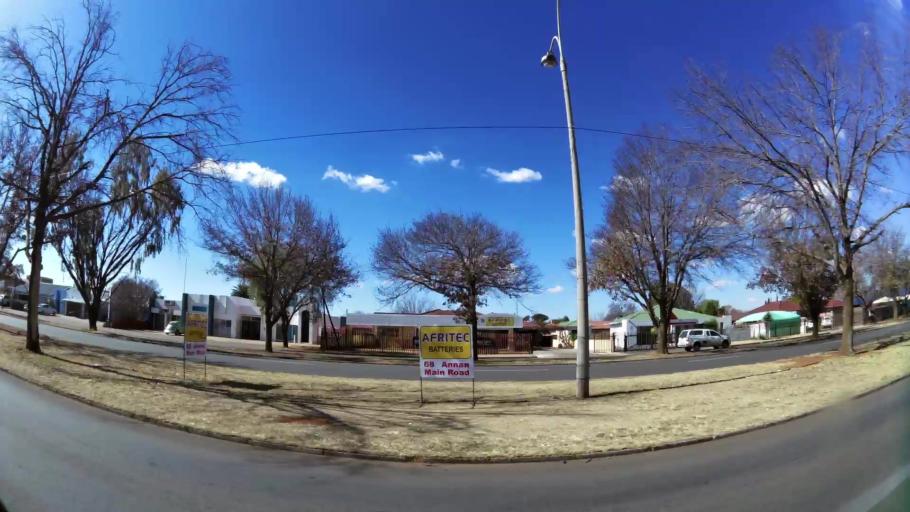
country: ZA
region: Gauteng
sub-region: West Rand District Municipality
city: Carletonville
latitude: -26.3588
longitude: 27.4006
